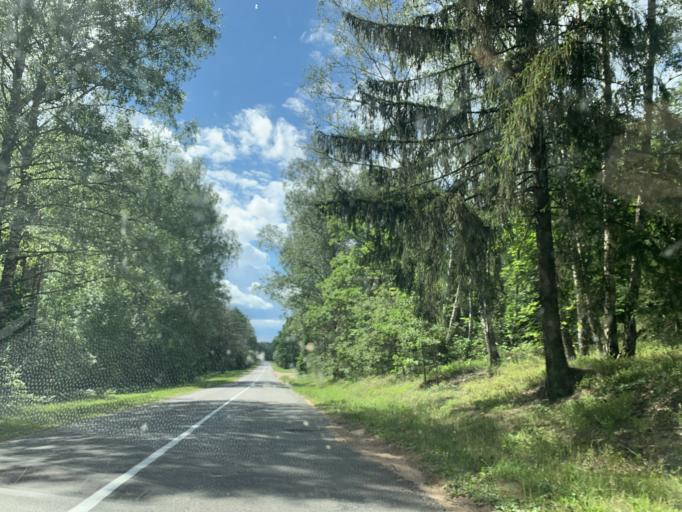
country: BY
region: Minsk
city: Rakaw
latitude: 53.9862
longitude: 26.9627
